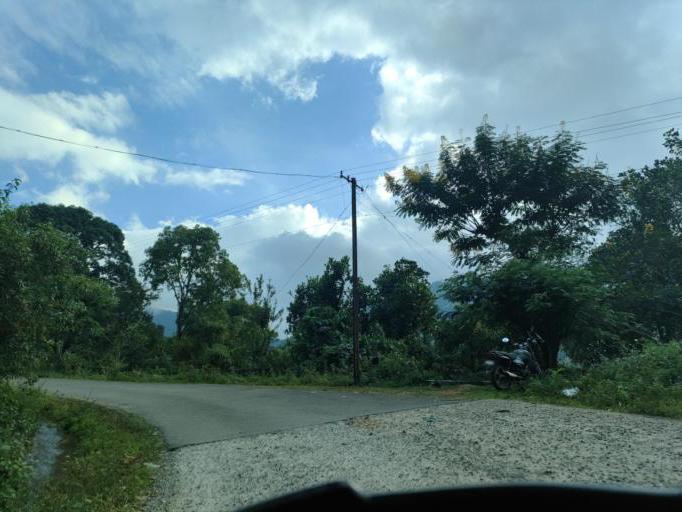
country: IN
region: Tamil Nadu
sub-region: Dindigul
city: Kodaikanal
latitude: 10.2777
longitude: 77.5322
